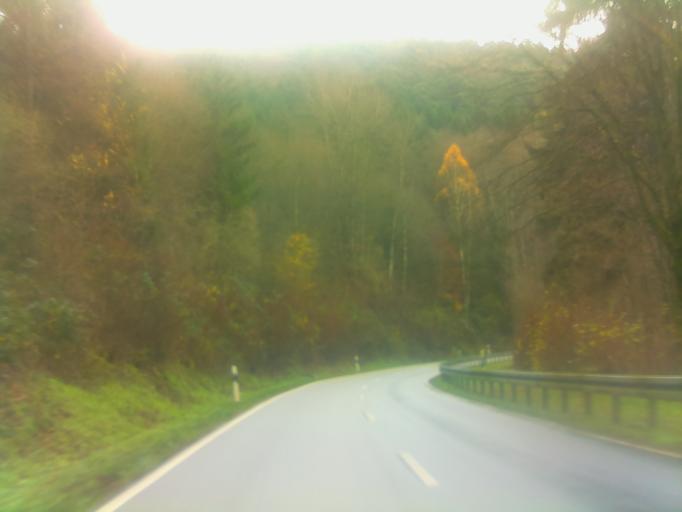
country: DE
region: Hesse
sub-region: Regierungsbezirk Darmstadt
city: Wald-Michelbach
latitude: 49.5537
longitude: 8.8538
